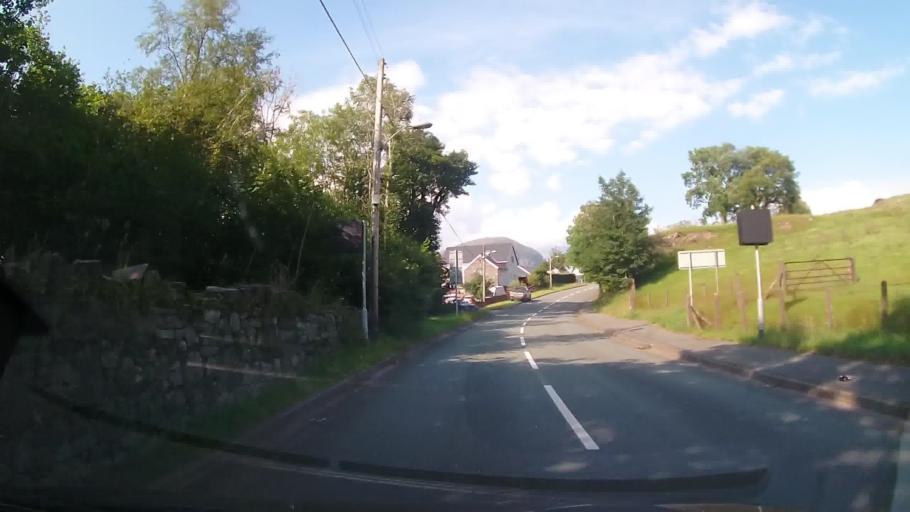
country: GB
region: Wales
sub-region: Gwynedd
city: Ffestiniog
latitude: 52.9589
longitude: -3.9300
